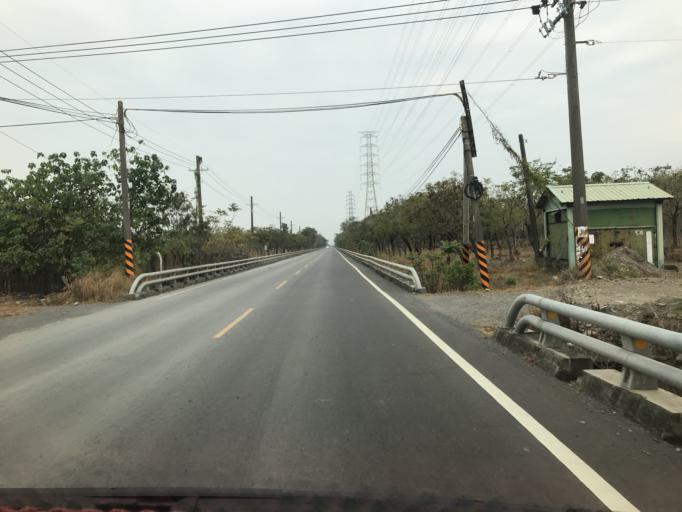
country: TW
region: Taiwan
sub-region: Pingtung
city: Pingtung
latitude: 22.4400
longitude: 120.6046
